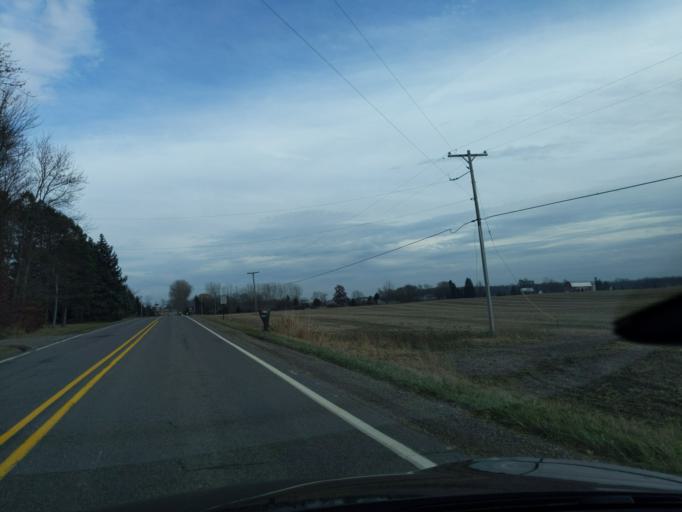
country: US
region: Michigan
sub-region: Ingham County
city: Mason
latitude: 42.6400
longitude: -84.3910
